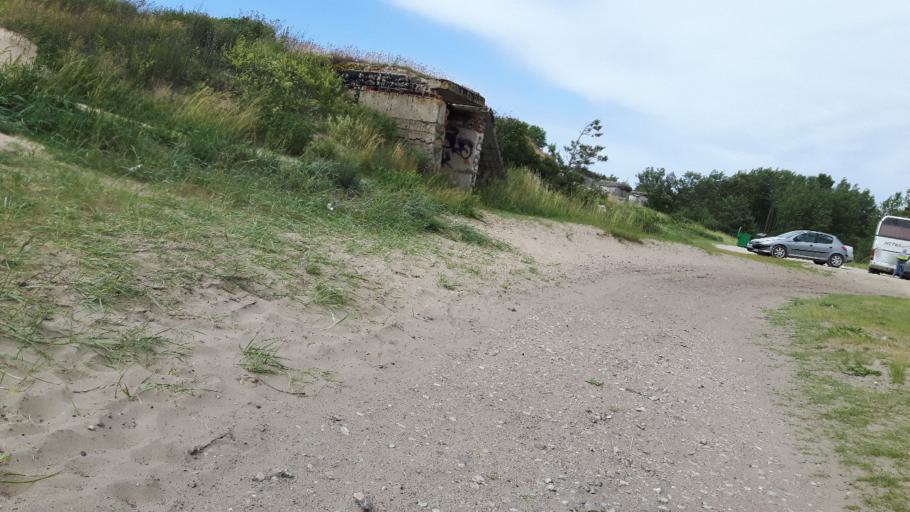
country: LV
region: Liepaja
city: Vec-Liepaja
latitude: 56.5910
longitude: 21.0155
